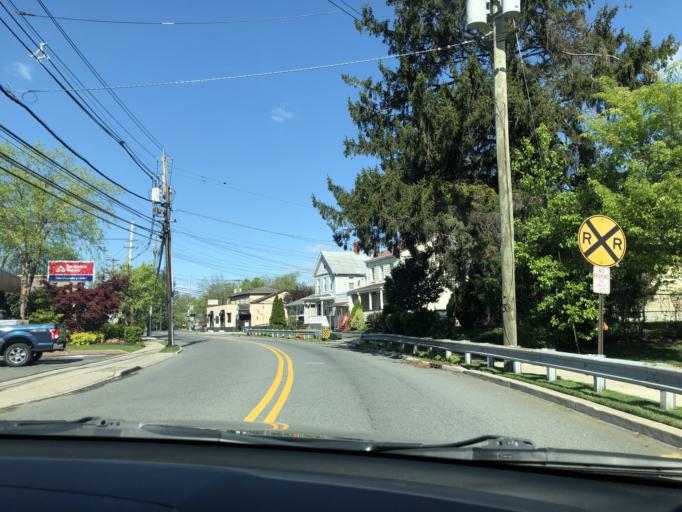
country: US
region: New Jersey
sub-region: Passaic County
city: Singac
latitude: 40.8864
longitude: -74.2416
